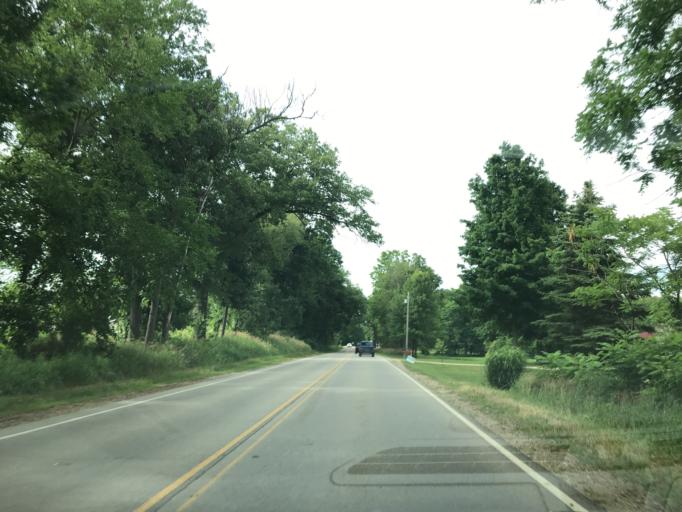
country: US
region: Michigan
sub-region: Jackson County
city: Spring Arbor
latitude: 42.0698
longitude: -84.5166
